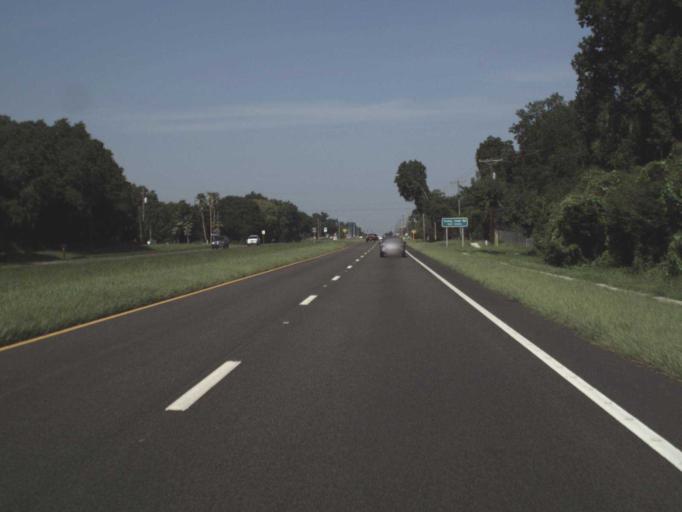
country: US
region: Florida
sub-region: Hillsborough County
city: Valrico
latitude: 27.9377
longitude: -82.1604
